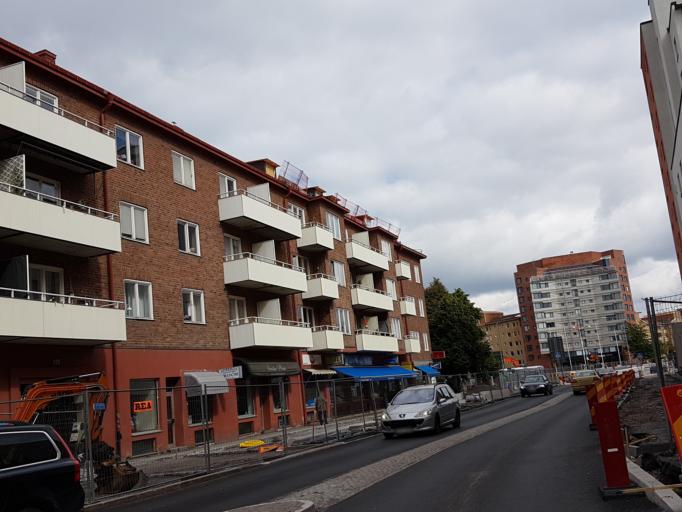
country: SE
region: Stockholm
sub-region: Sundbybergs Kommun
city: Sundbyberg
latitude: 59.3644
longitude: 17.9760
